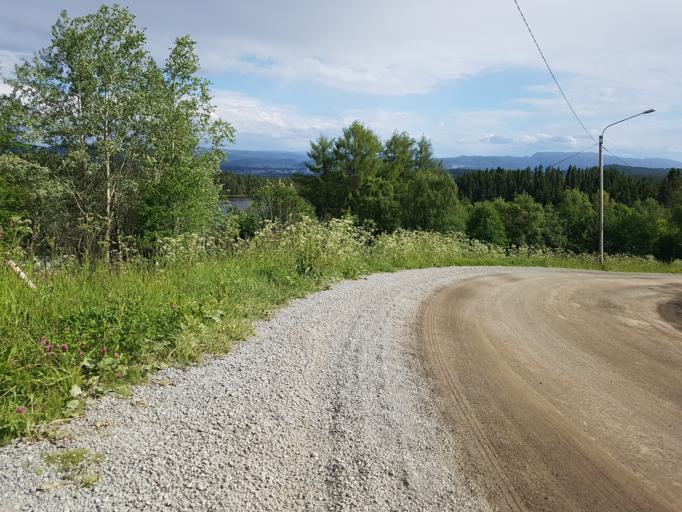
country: NO
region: Sor-Trondelag
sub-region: Trondheim
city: Trondheim
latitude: 63.4032
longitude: 10.3120
